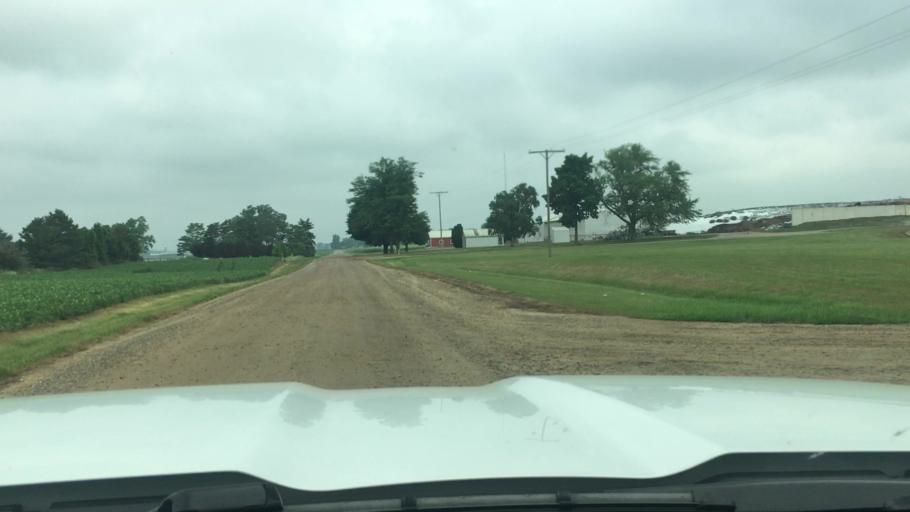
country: US
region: Michigan
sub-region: Sanilac County
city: Marlette
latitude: 43.3470
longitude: -82.9754
